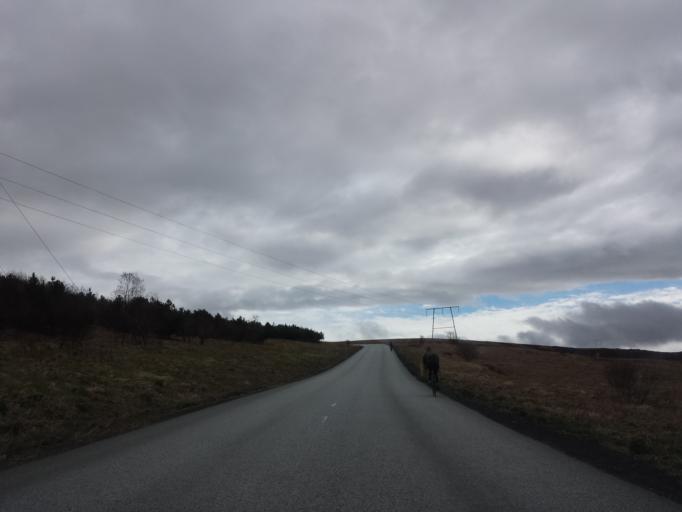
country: IS
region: Capital Region
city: Kopavogur
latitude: 64.0812
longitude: -21.8649
